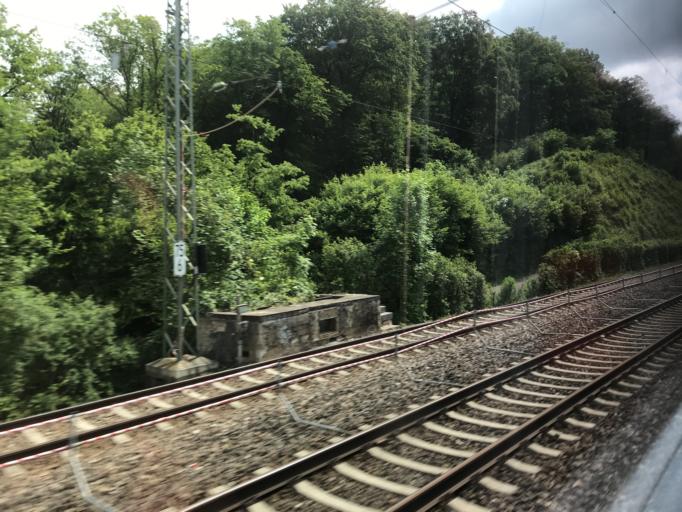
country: DE
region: Baden-Wuerttemberg
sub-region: Tuebingen Region
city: Westerstetten
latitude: 48.5270
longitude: 9.9391
